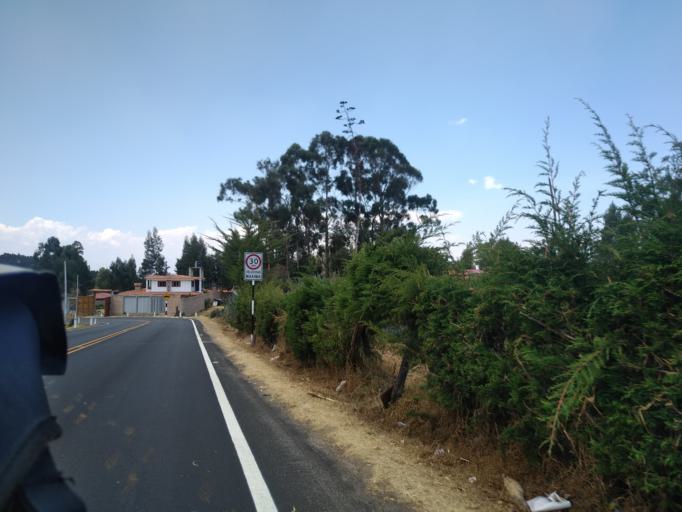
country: PE
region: Cajamarca
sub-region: San Marcos
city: San Marcos
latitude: -7.2788
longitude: -78.2380
